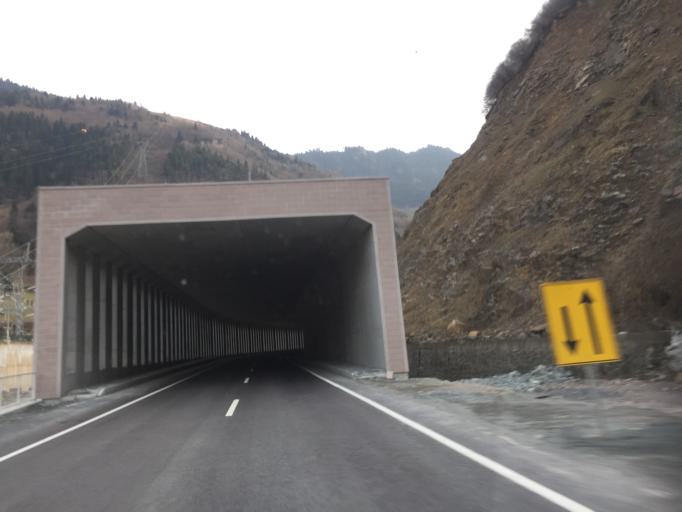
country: TR
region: Trabzon
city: Macka
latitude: 40.7539
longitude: 39.5635
